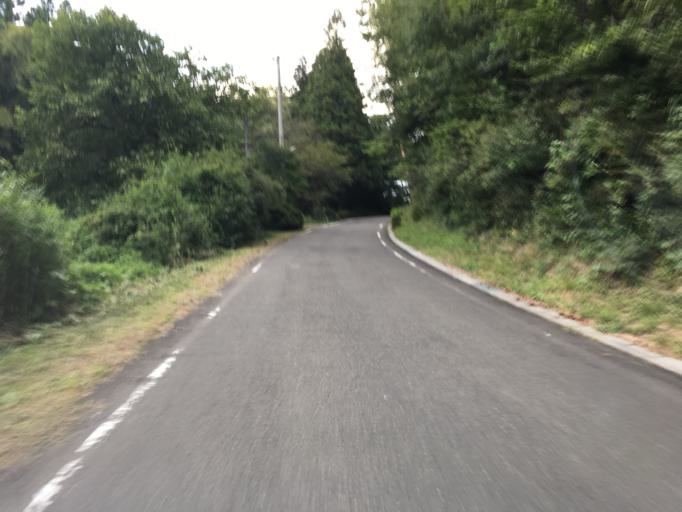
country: JP
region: Fukushima
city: Fukushima-shi
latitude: 37.6684
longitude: 140.4608
